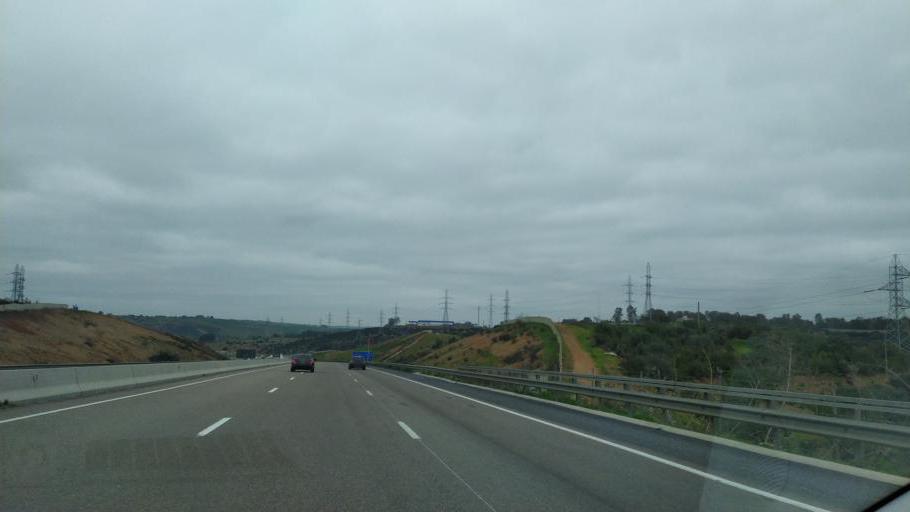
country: MA
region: Rabat-Sale-Zemmour-Zaer
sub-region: Rabat
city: Rabat
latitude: 33.9232
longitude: -6.7666
